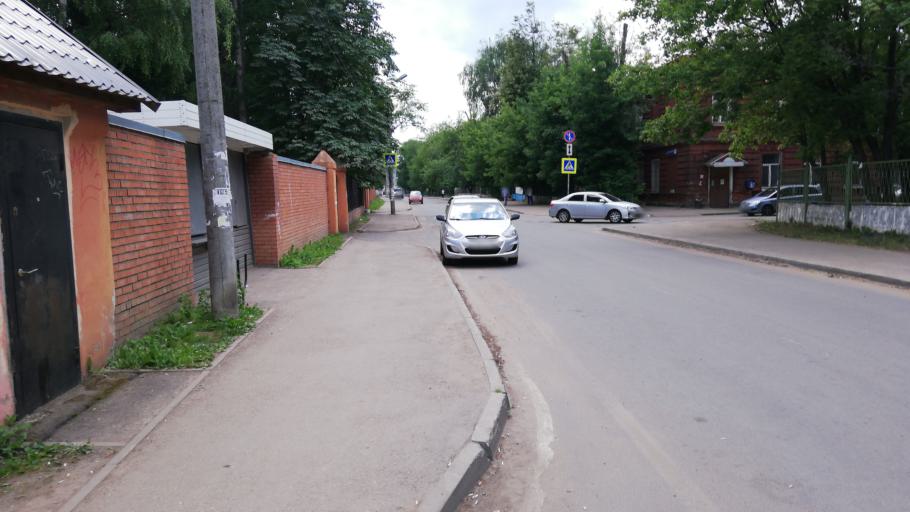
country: RU
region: Jaroslavl
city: Yaroslavl
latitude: 57.6391
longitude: 39.8650
